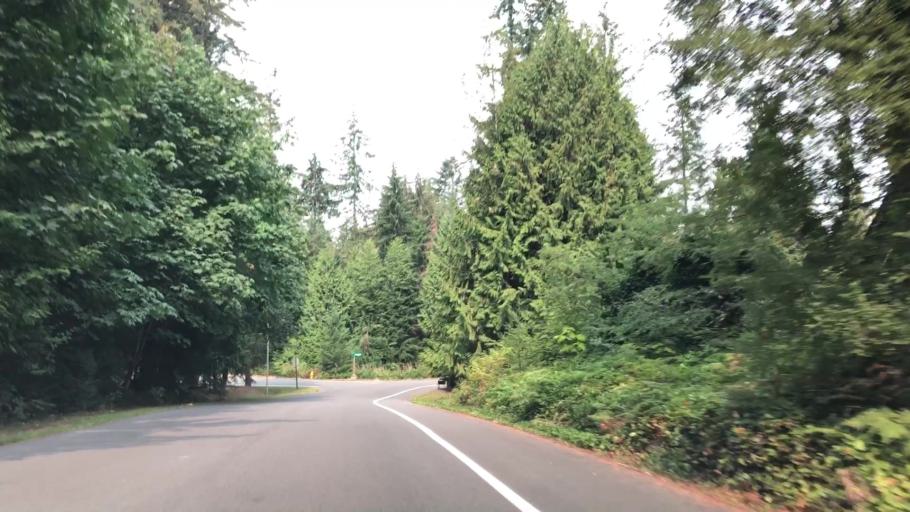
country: US
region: Washington
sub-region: King County
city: Cottage Lake
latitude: 47.7722
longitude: -122.0797
